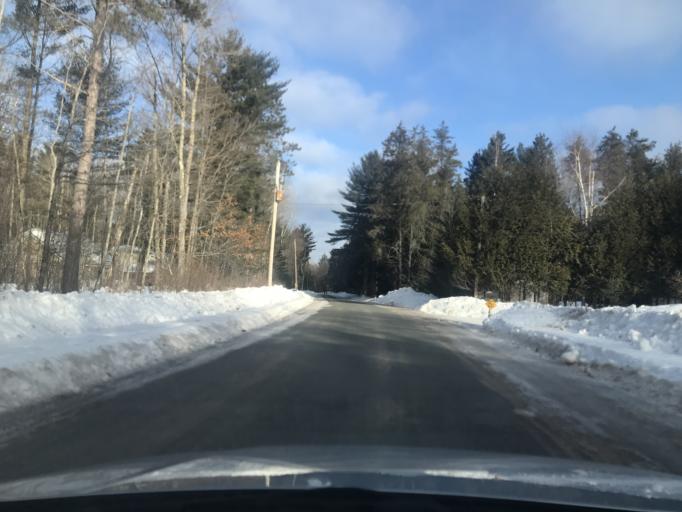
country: US
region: Wisconsin
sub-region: Marinette County
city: Niagara
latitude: 45.6331
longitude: -87.9680
